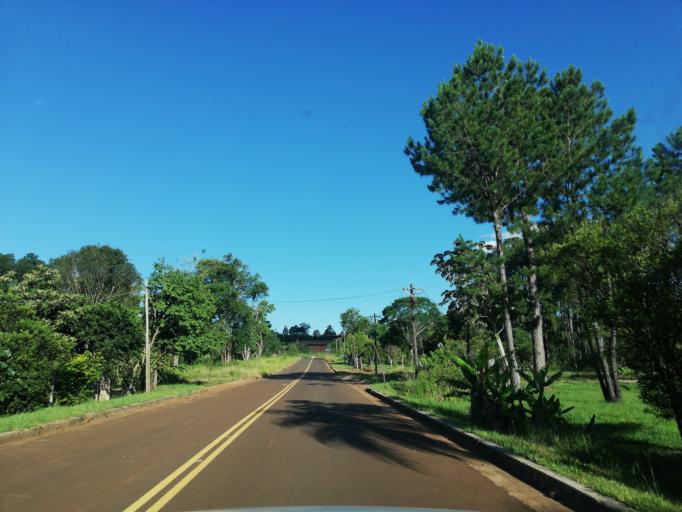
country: AR
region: Misiones
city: Garupa
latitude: -27.4647
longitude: -55.7995
